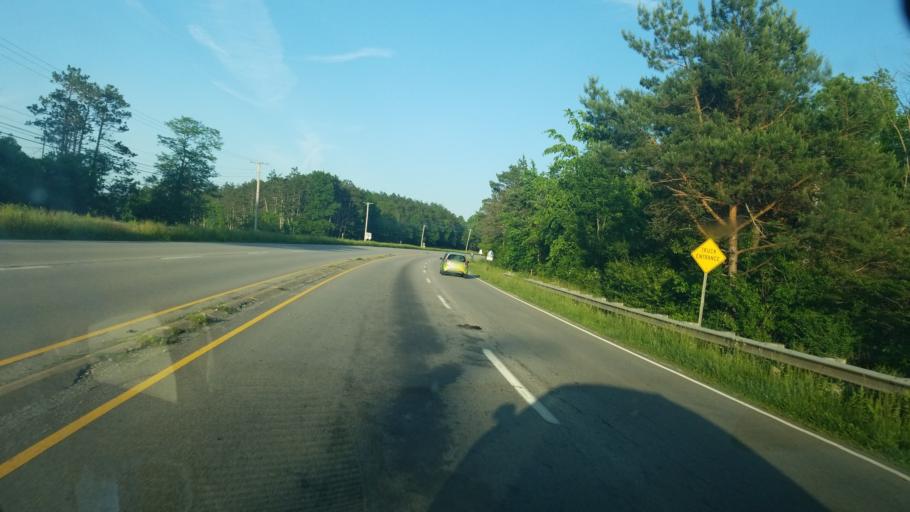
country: US
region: Ohio
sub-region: Mahoning County
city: Austintown
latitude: 41.1002
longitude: -80.8225
